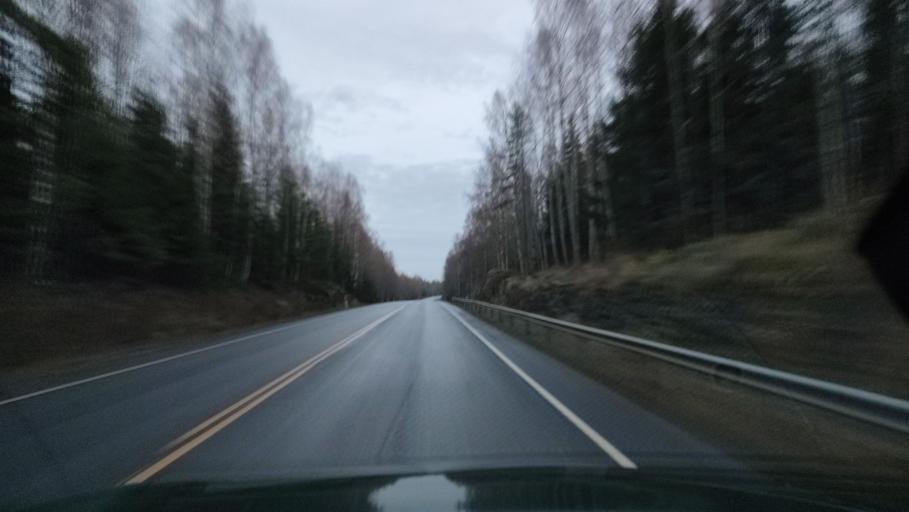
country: FI
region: Ostrobothnia
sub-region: Vaasa
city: Ristinummi
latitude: 62.9839
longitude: 21.7682
